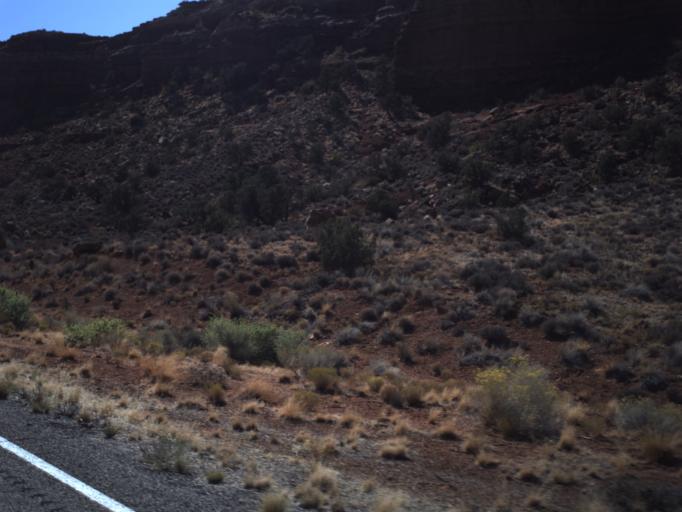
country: US
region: Utah
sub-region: San Juan County
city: Blanding
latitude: 37.7227
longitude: -110.2488
